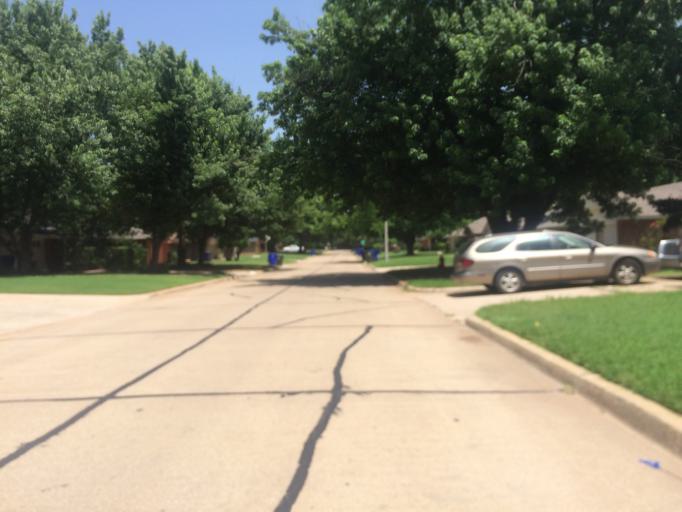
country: US
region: Oklahoma
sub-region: Cleveland County
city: Norman
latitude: 35.2015
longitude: -97.4614
